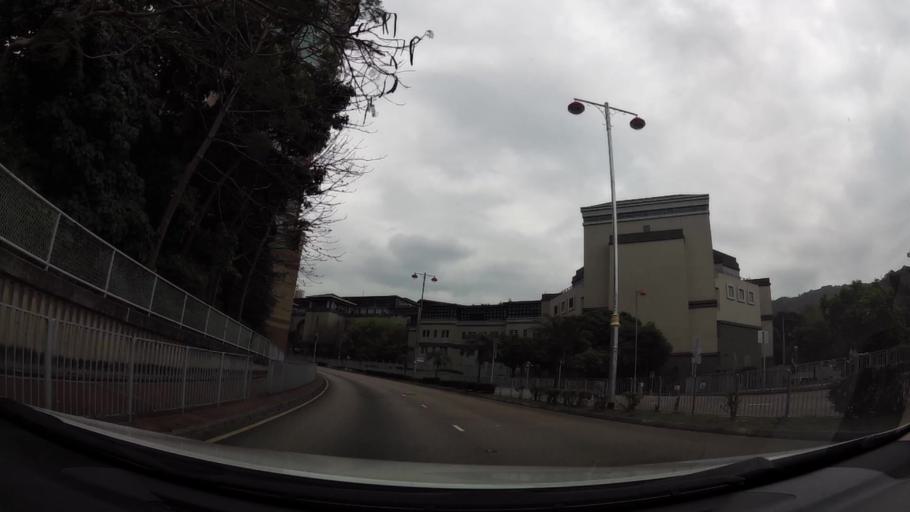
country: HK
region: Tuen Mun
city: Tuen Mun
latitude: 22.4091
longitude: 113.9815
